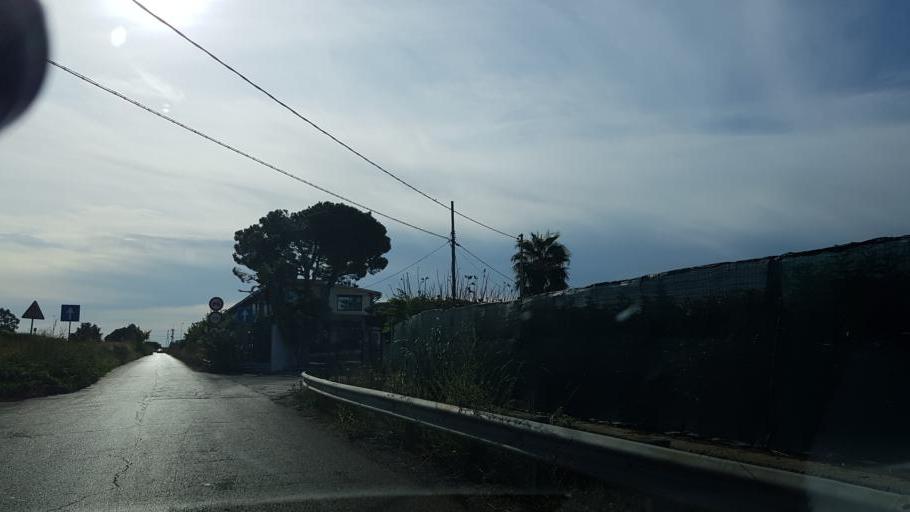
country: IT
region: Apulia
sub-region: Provincia di Brindisi
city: La Rosa
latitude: 40.6161
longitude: 17.9535
